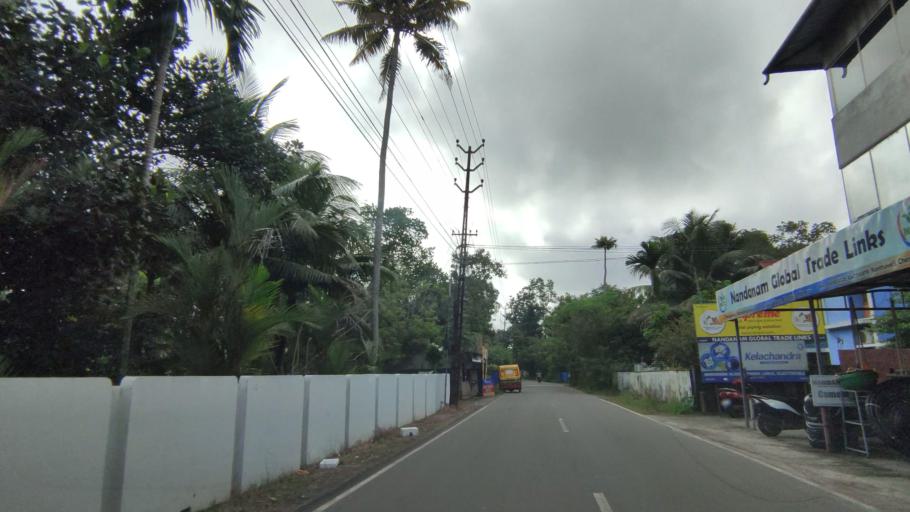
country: IN
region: Kerala
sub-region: Alappuzha
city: Shertallai
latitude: 9.6401
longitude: 76.3464
